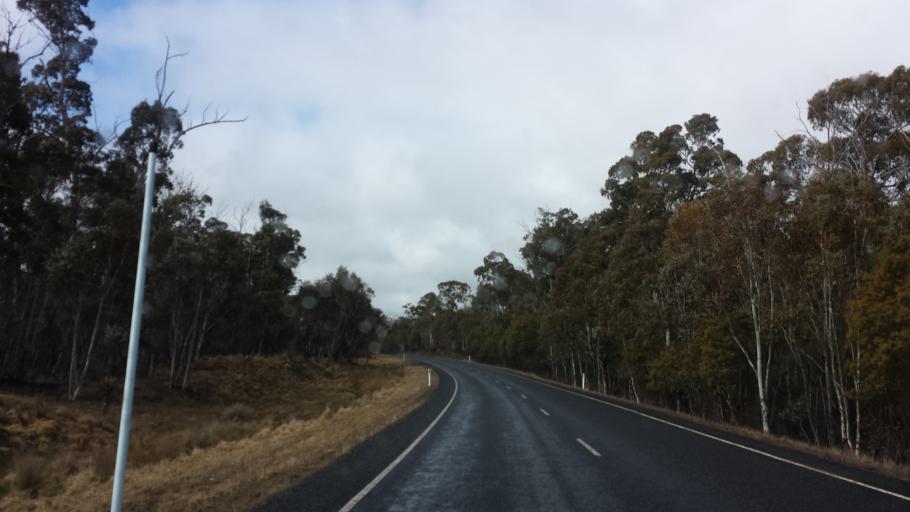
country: AU
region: Victoria
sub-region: Alpine
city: Mount Beauty
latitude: -37.0677
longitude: 147.3428
